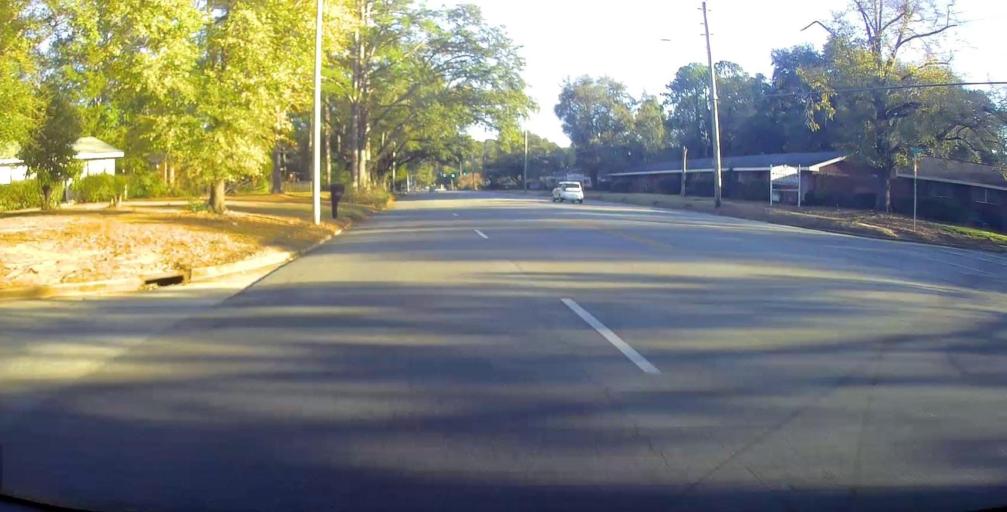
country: US
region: Georgia
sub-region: Dougherty County
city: Albany
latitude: 31.5987
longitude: -84.1650
